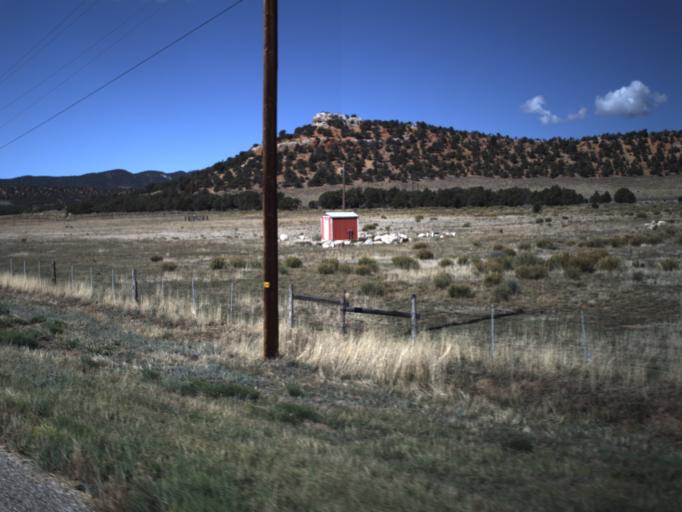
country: US
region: Utah
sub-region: Iron County
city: Cedar City
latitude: 37.6330
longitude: -113.2944
